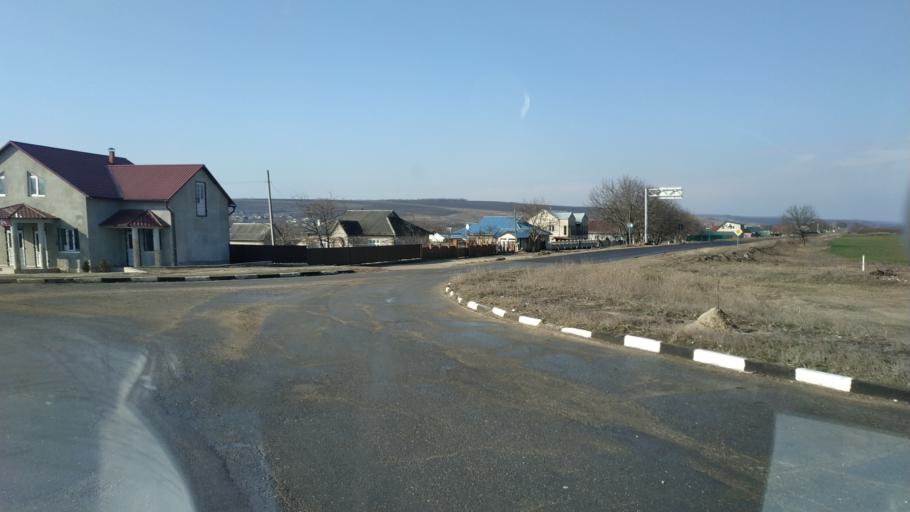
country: MD
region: Chisinau
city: Singera
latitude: 46.6879
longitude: 29.0521
